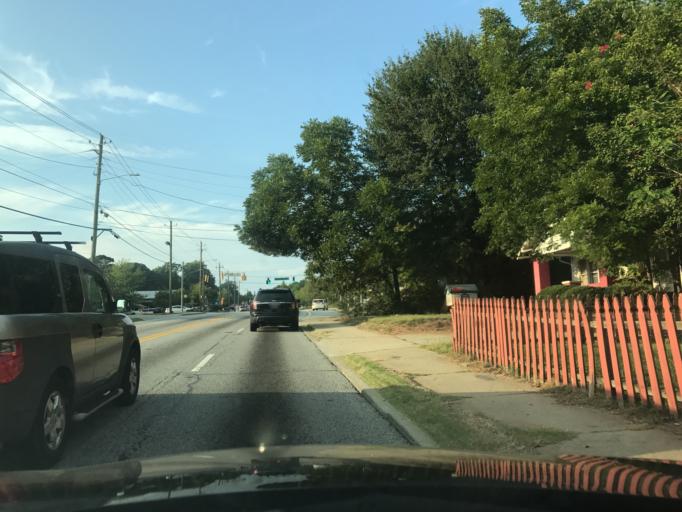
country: US
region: Georgia
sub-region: DeKalb County
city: Gresham Park
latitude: 33.7209
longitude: -84.3494
